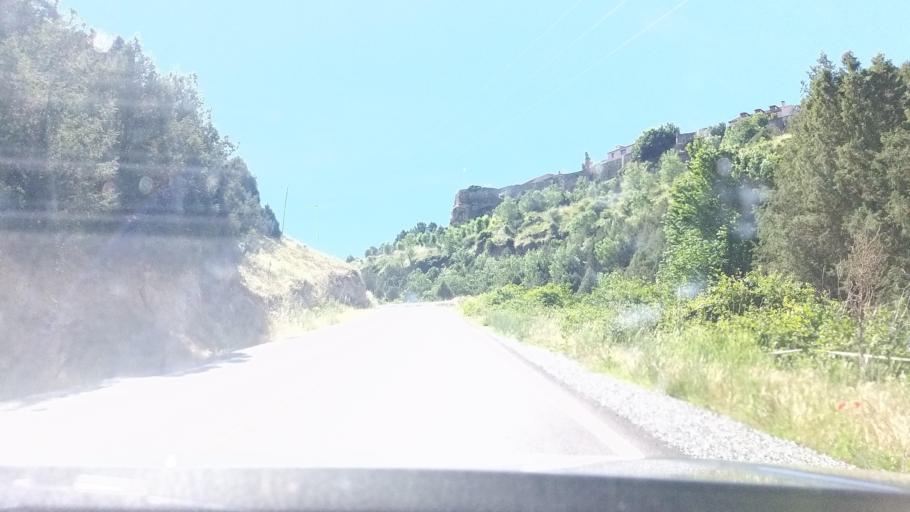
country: ES
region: Castille and Leon
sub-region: Provincia de Segovia
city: Pedraza
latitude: 41.1338
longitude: -3.8133
